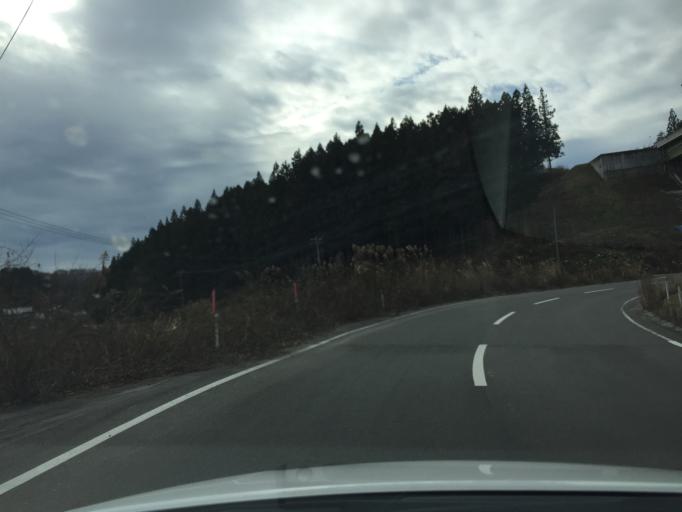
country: JP
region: Fukushima
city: Funehikimachi-funehiki
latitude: 37.2907
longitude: 140.6078
